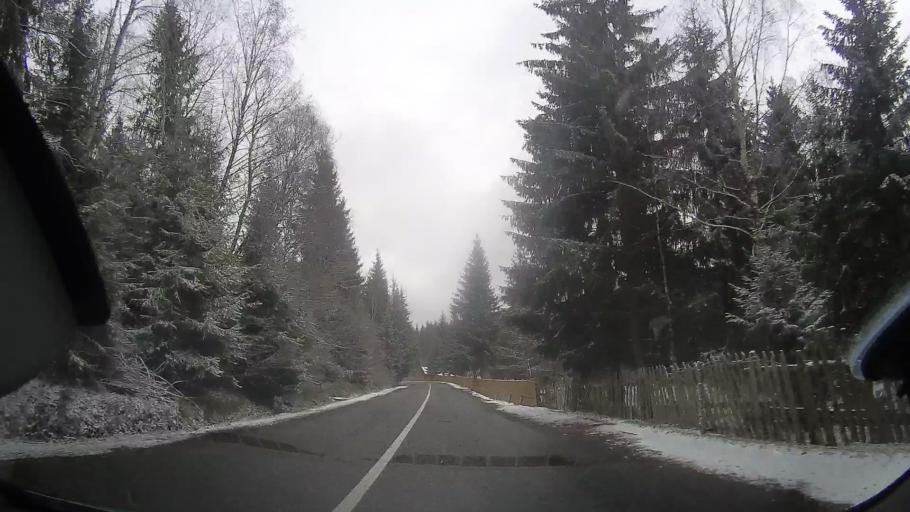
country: RO
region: Cluj
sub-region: Comuna Calatele
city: Calatele
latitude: 46.7144
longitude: 23.0431
